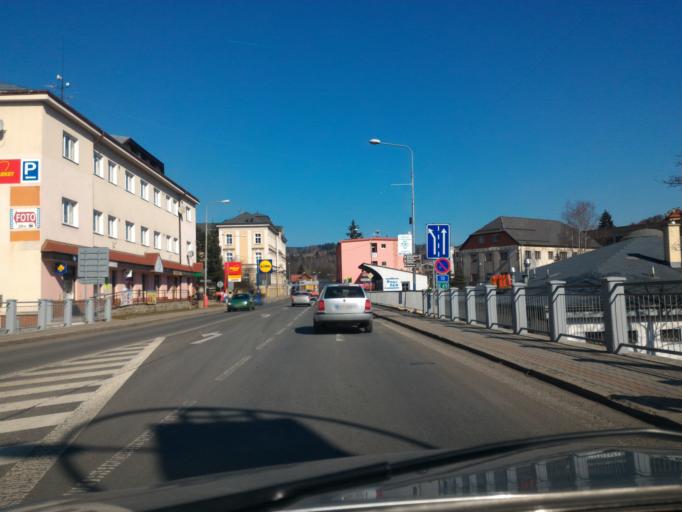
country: CZ
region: Liberecky
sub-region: Okres Jablonec nad Nisou
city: Tanvald
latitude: 50.7359
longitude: 15.3082
